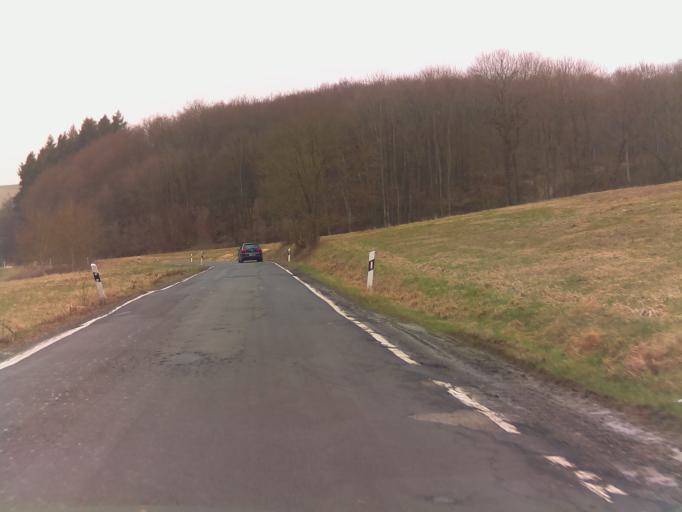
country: DE
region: Rheinland-Pfalz
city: Abtweiler
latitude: 49.7366
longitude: 7.6510
